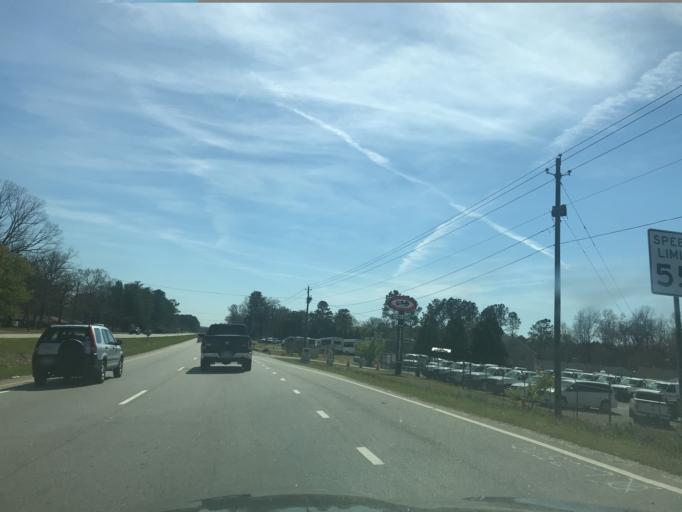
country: US
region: North Carolina
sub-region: Wake County
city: Garner
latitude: 35.6626
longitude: -78.7026
